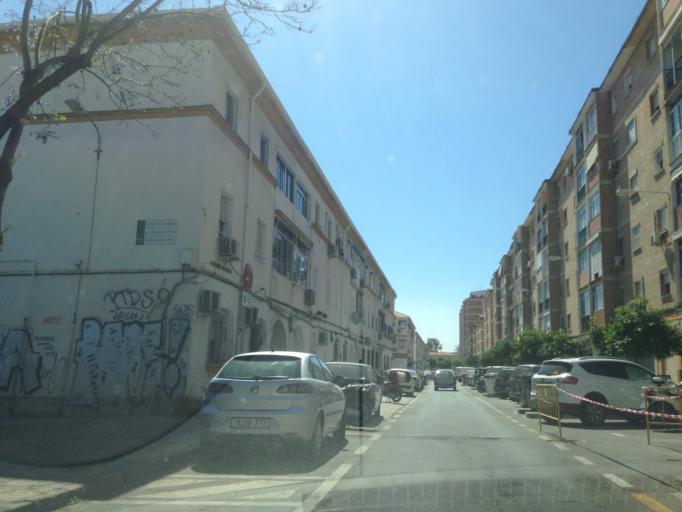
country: ES
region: Andalusia
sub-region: Provincia de Malaga
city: Malaga
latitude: 36.6985
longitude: -4.4451
